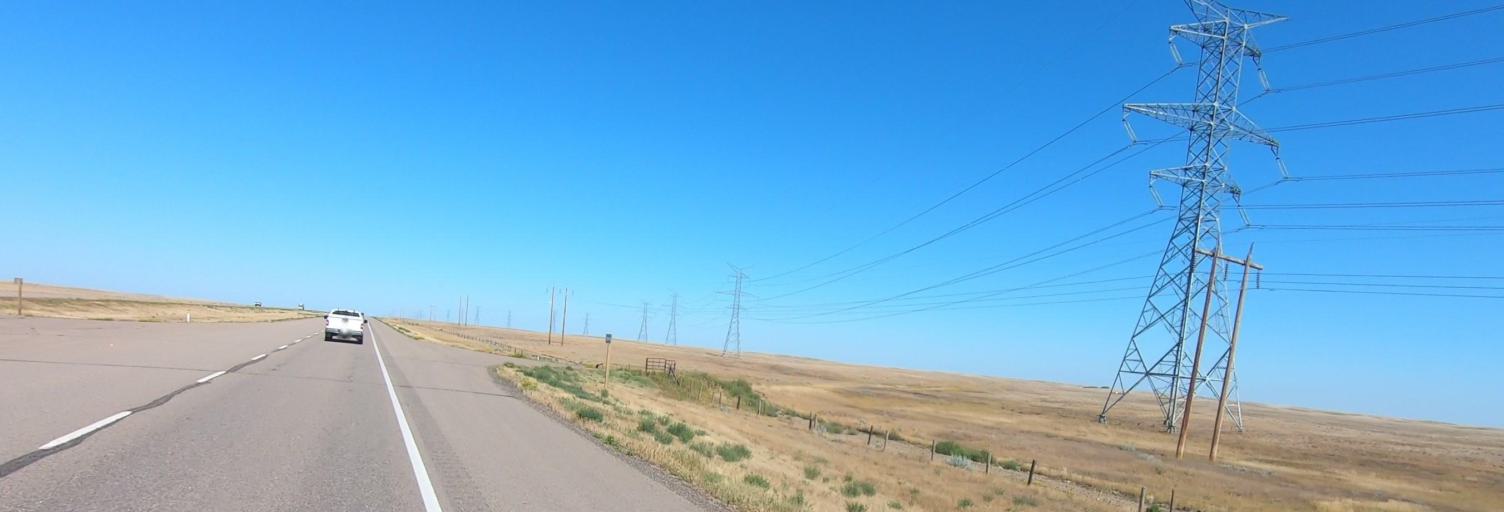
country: CA
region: Alberta
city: Bow Island
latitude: 50.2975
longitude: -111.3104
